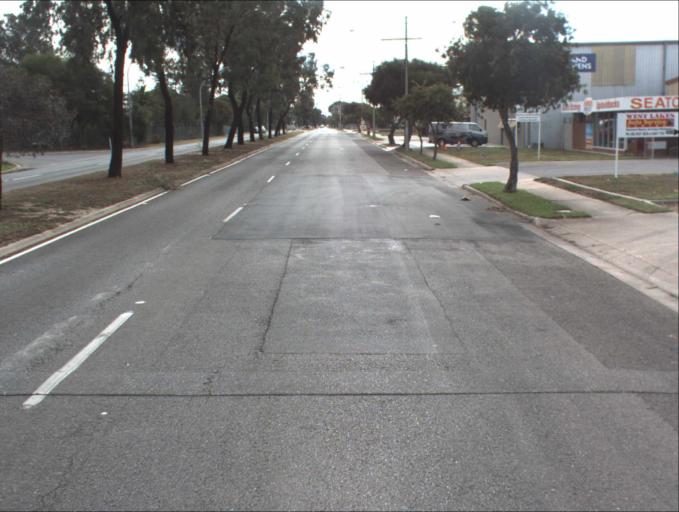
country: AU
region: South Australia
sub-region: Charles Sturt
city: Royal Park
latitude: -34.8673
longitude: 138.5030
